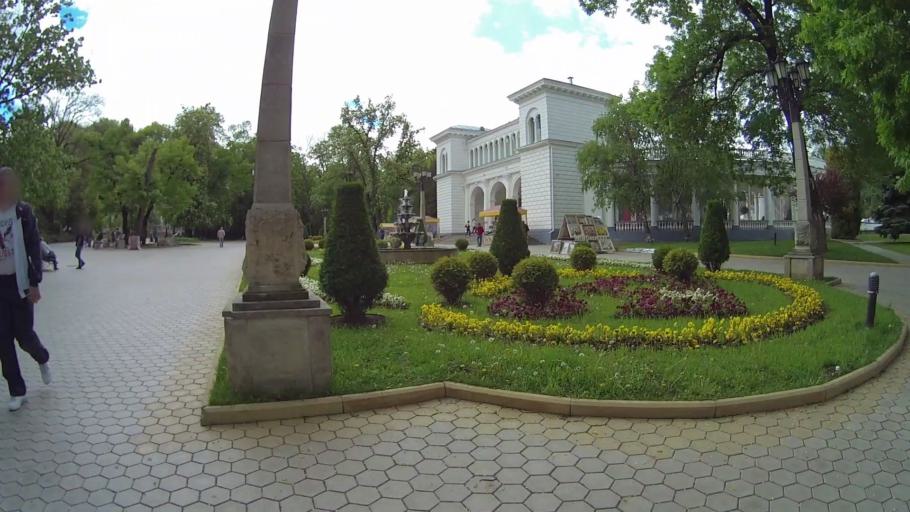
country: RU
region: Stavropol'skiy
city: Kislovodsk
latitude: 43.8991
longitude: 42.7171
